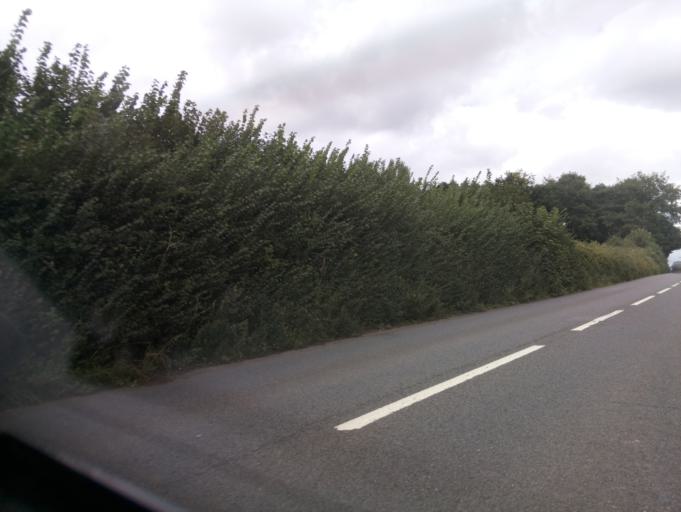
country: GB
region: England
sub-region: Devon
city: Heavitree
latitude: 50.7607
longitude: -3.4424
